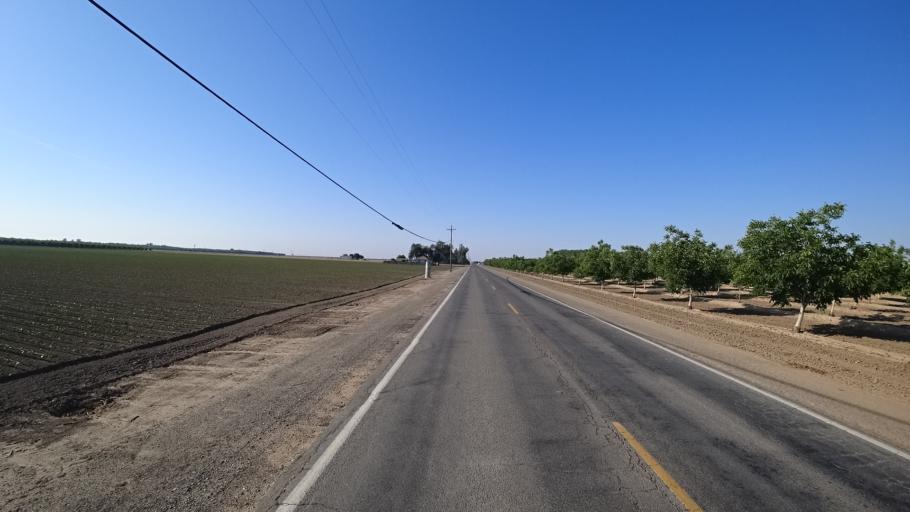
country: US
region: California
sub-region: Kings County
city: Armona
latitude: 36.2609
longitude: -119.7090
